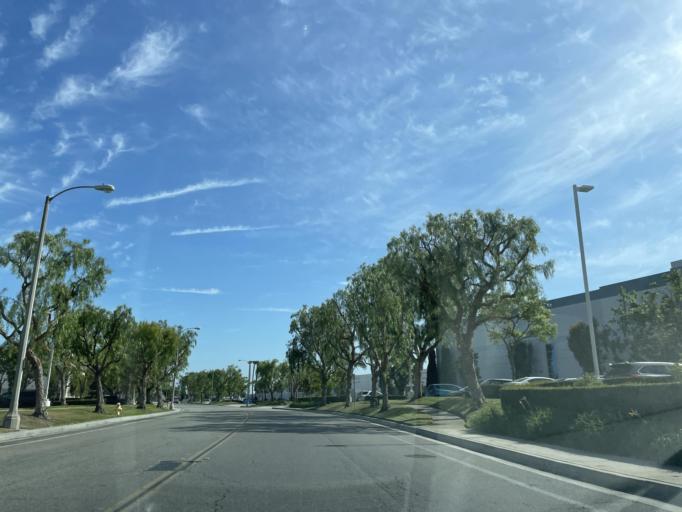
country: US
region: California
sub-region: Los Angeles County
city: Norwalk
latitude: 33.9143
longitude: -118.0507
